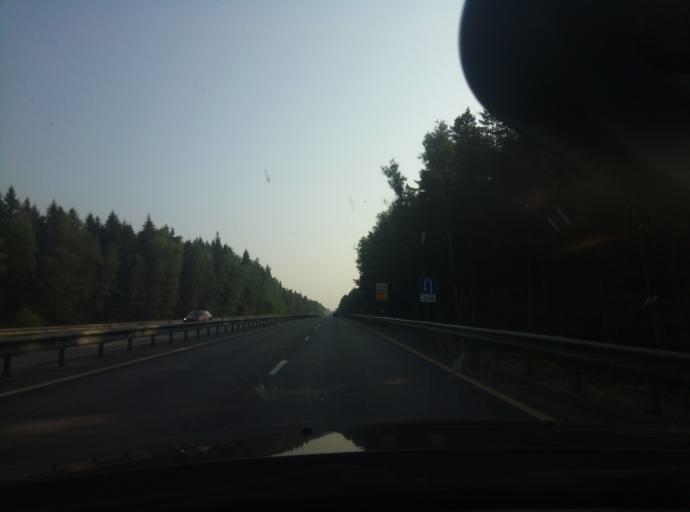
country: RU
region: Kaluga
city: Maloyaroslavets
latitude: 54.9975
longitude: 36.5234
